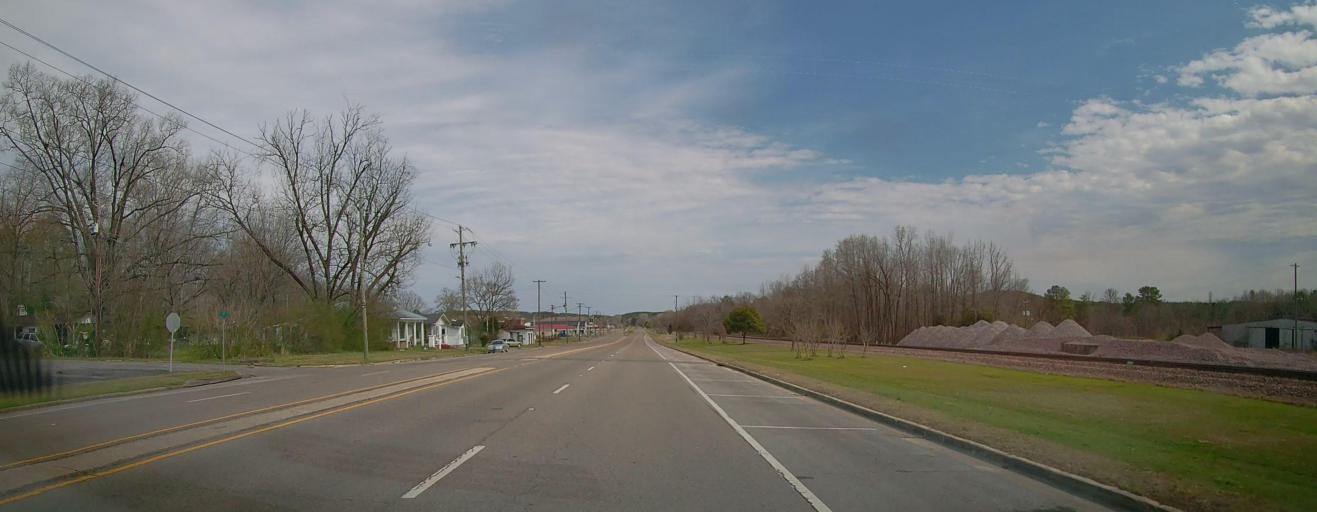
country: US
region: Alabama
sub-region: Walker County
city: Carbon Hill
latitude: 33.8878
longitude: -87.5270
